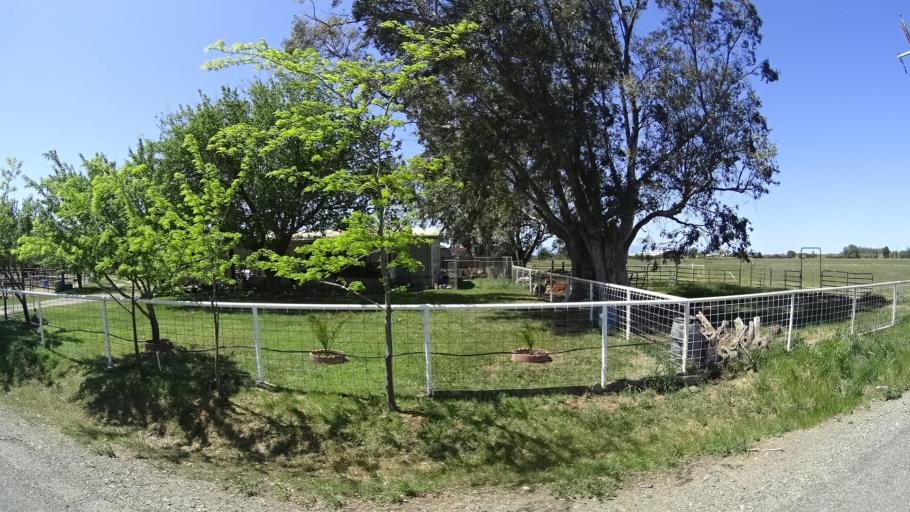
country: US
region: California
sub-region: Glenn County
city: Orland
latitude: 39.7876
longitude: -122.1784
